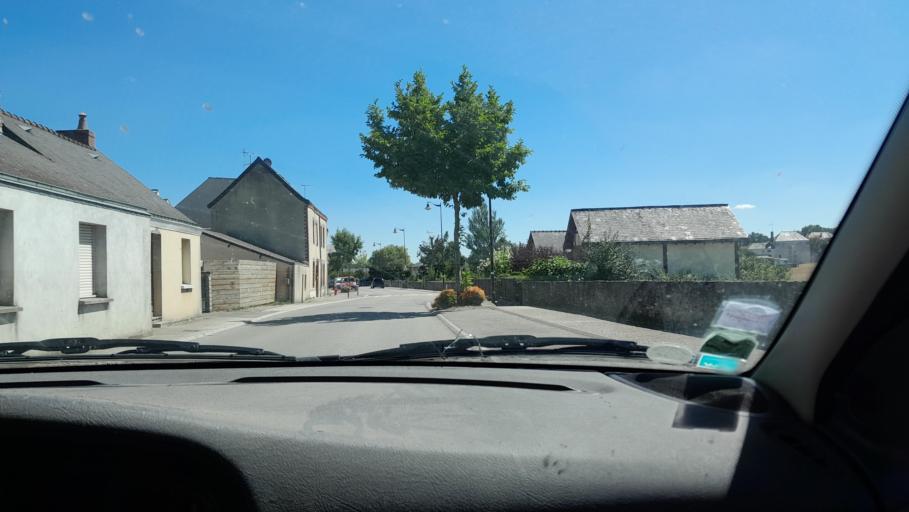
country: FR
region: Pays de la Loire
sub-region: Departement de Maine-et-Loire
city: Pouance
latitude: 47.7396
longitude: -1.1790
